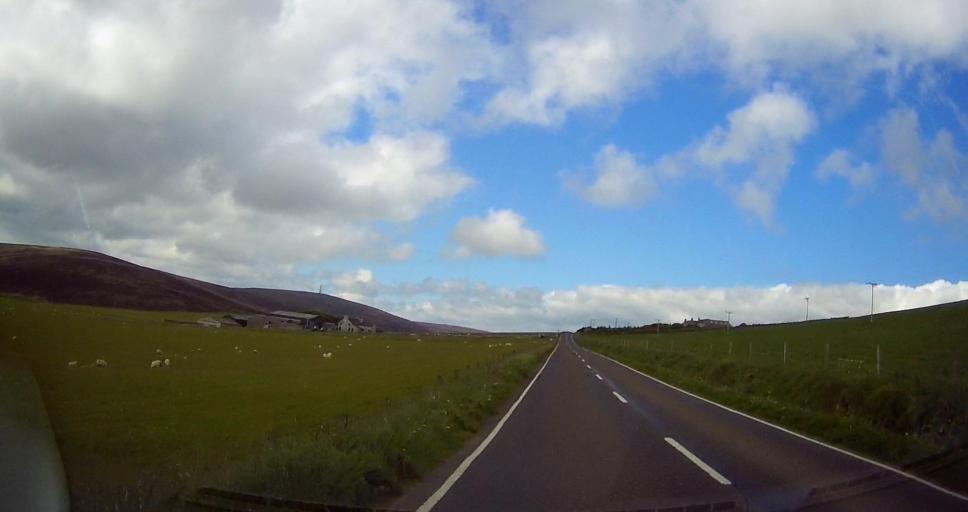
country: GB
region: Scotland
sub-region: Orkney Islands
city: Orkney
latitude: 58.9796
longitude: -3.0284
